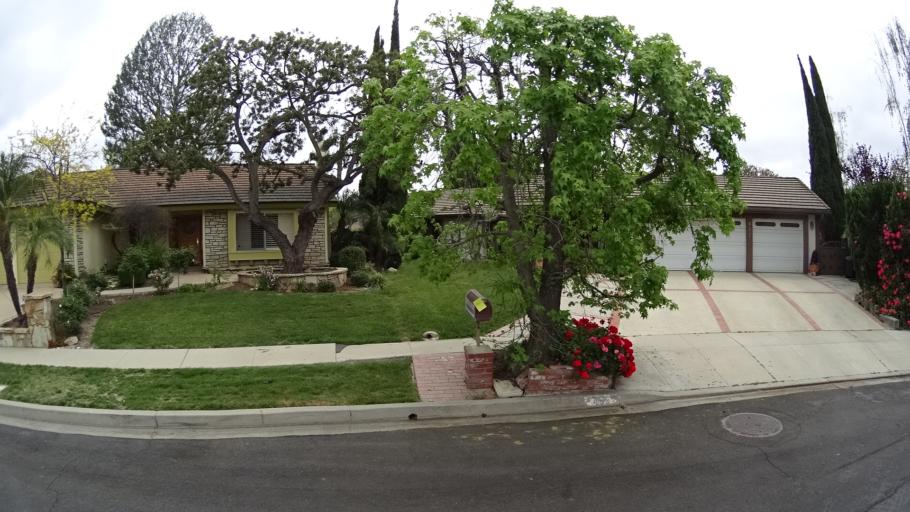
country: US
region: California
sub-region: Ventura County
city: Thousand Oaks
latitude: 34.2160
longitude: -118.8701
